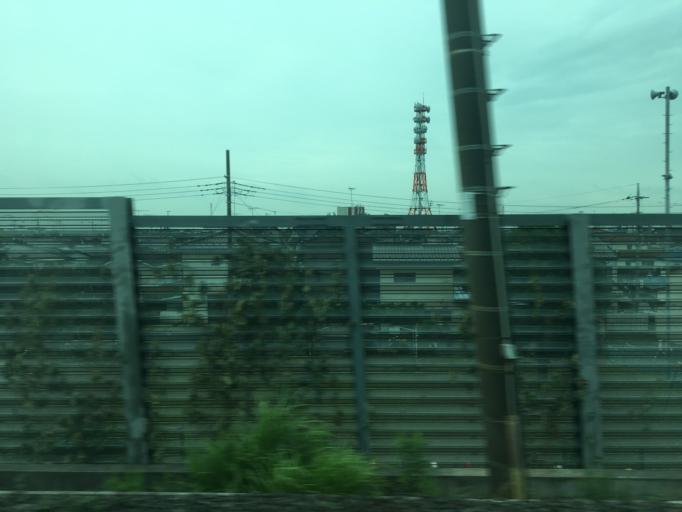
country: JP
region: Saitama
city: Kurihashi
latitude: 36.1448
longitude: 139.6964
